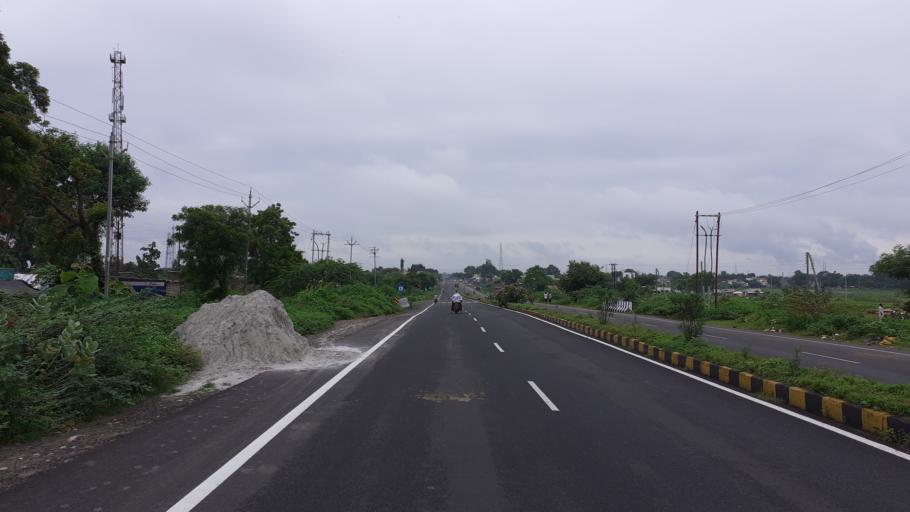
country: IN
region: Maharashtra
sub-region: Chandrapur
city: Warora
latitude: 20.3515
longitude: 79.0206
